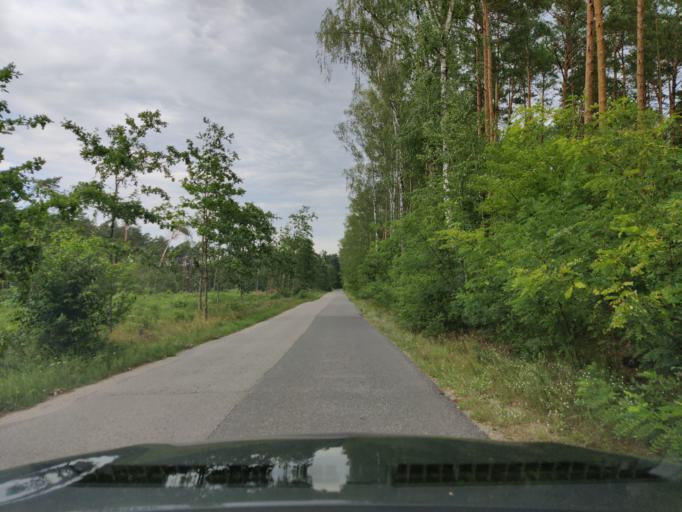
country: PL
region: Masovian Voivodeship
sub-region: Powiat pultuski
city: Pultusk
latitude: 52.7317
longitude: 21.1374
